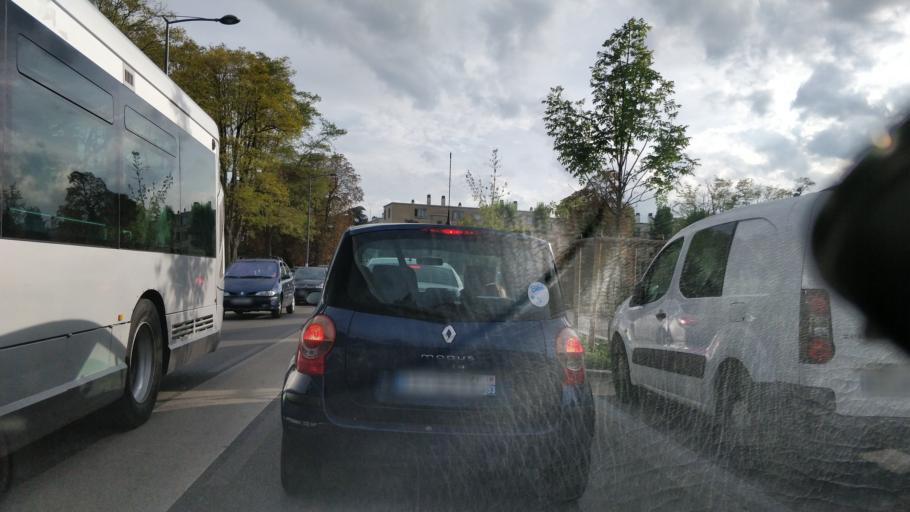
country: FR
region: Ile-de-France
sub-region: Departement de Seine-Saint-Denis
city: Clichy-sous-Bois
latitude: 48.9108
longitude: 2.5497
